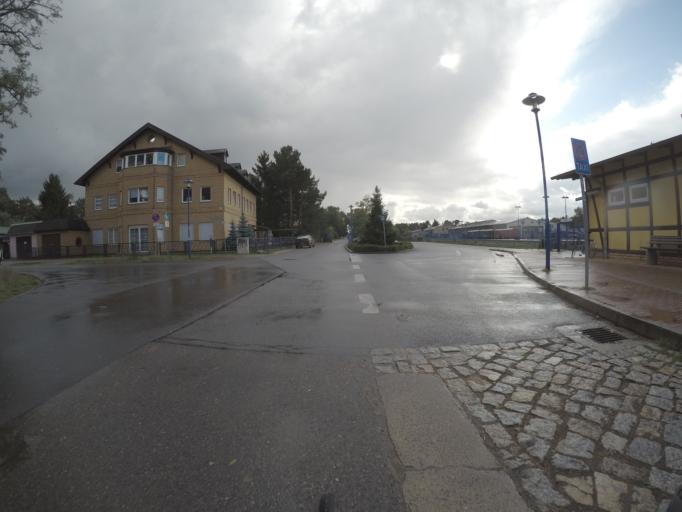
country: DE
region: Brandenburg
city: Wandlitz
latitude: 52.7154
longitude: 13.4343
